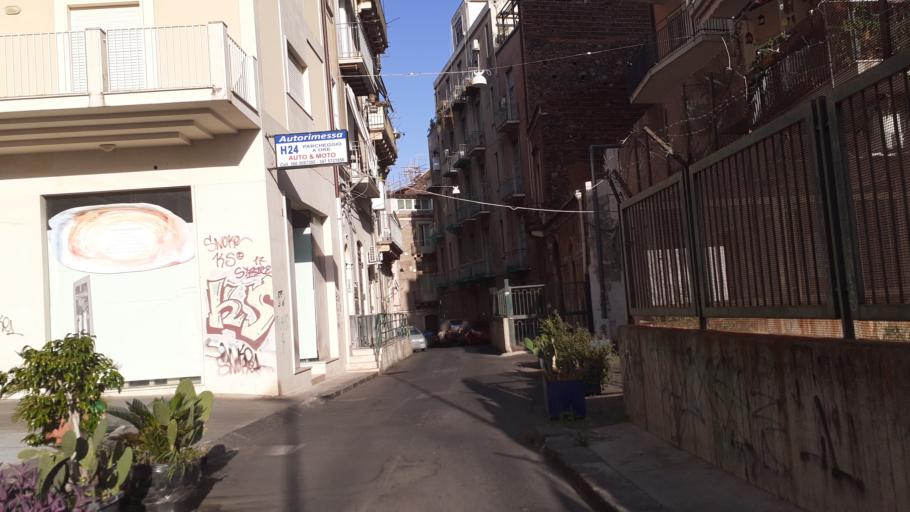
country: IT
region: Sicily
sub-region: Catania
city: Catania
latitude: 37.5130
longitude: 15.0873
